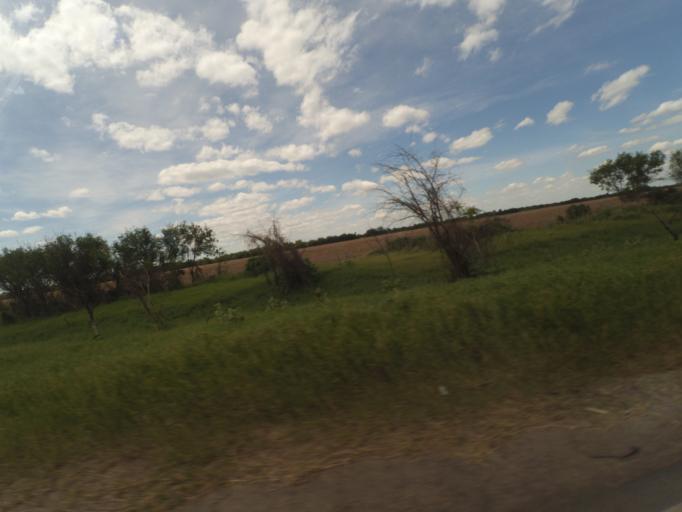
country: BO
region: Santa Cruz
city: Pailon
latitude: -17.5857
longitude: -62.0483
